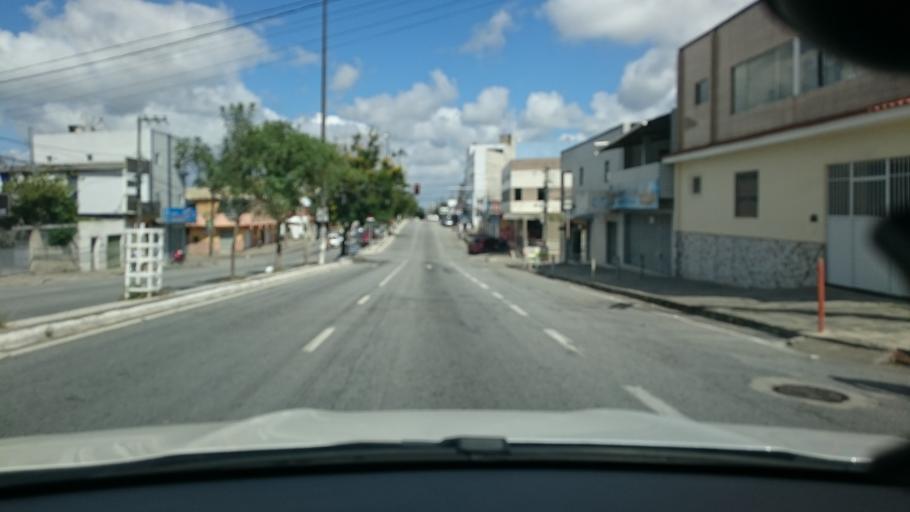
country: BR
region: Paraiba
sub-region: Campina Grande
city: Campina Grande
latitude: -7.2282
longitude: -35.9029
